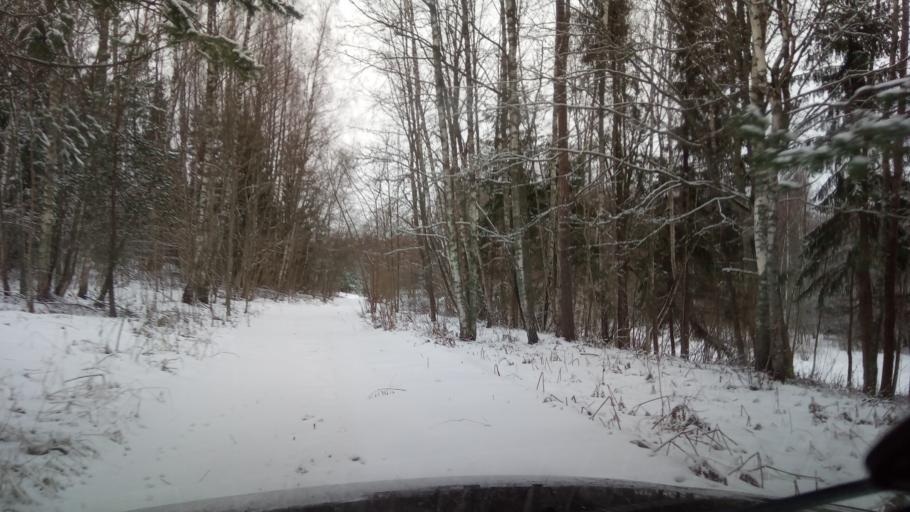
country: LT
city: Zarasai
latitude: 55.6624
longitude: 26.0945
